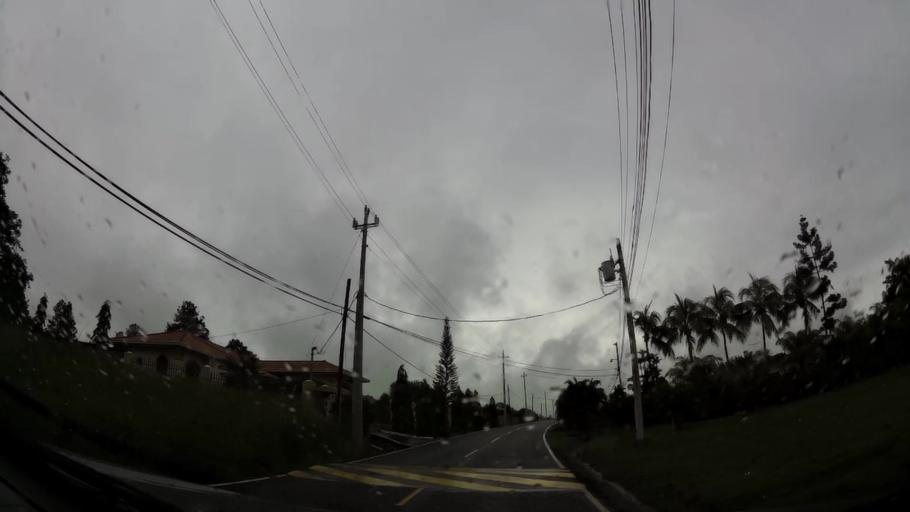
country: PA
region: Veraguas
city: Santiago de Veraguas
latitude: 8.0924
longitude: -80.9583
